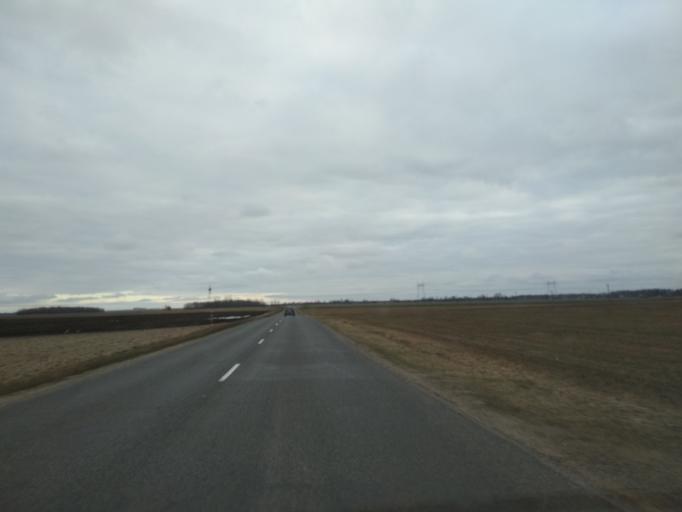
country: BY
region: Minsk
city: Mar''ina Horka
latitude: 53.5613
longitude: 28.0437
